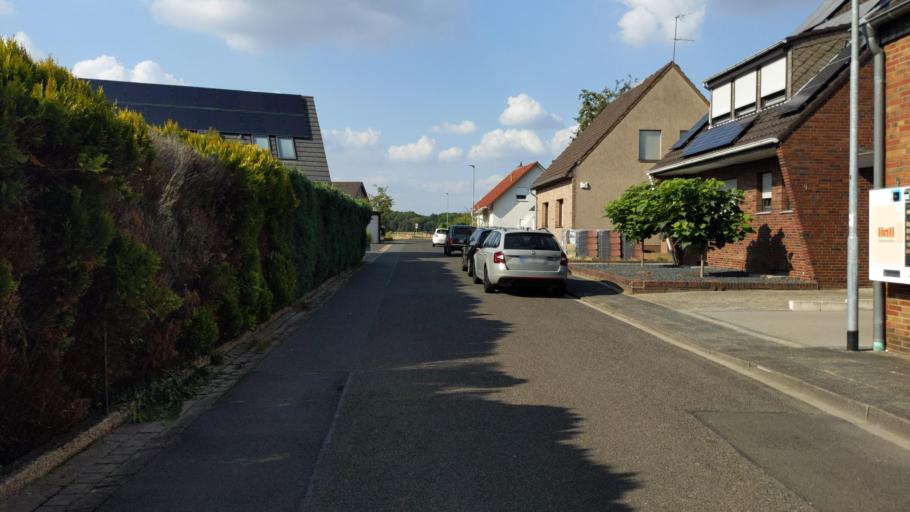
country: DE
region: North Rhine-Westphalia
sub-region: Regierungsbezirk Dusseldorf
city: Kaarst
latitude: 51.2177
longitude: 6.5747
